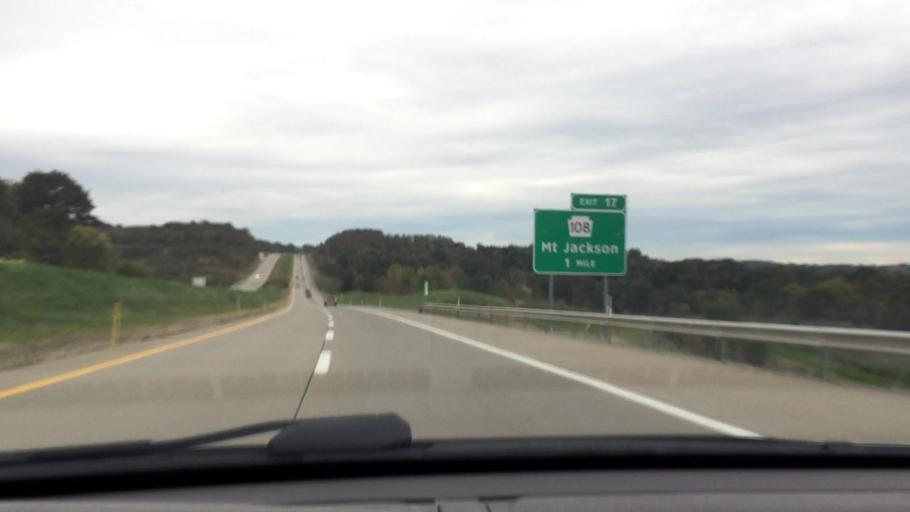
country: US
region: Pennsylvania
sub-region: Lawrence County
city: Oakland
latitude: 40.9529
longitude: -80.3930
